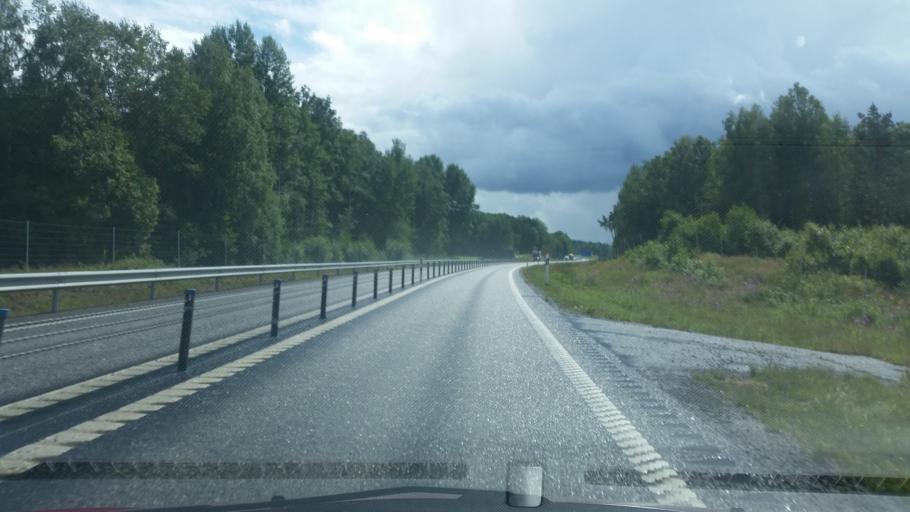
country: SE
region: Joenkoeping
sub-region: Gislaveds Kommun
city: Gislaved
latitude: 57.2679
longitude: 13.6268
